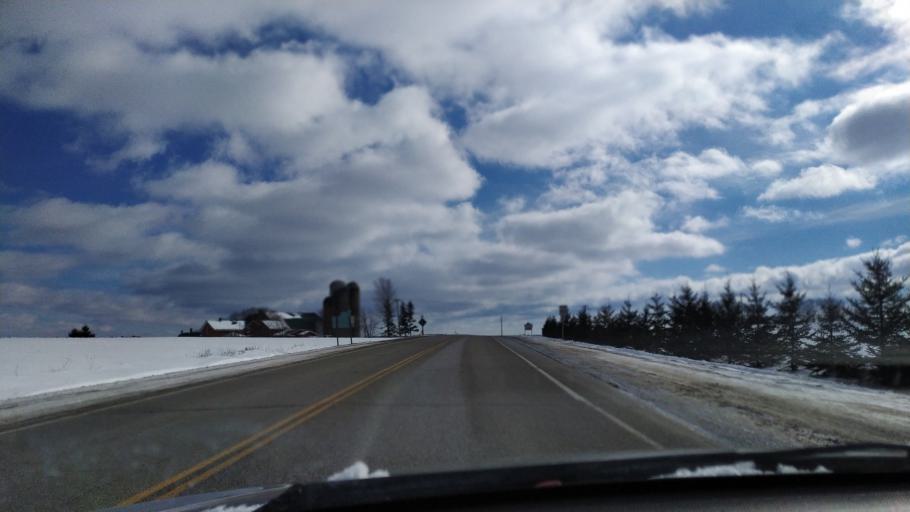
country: CA
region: Ontario
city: Waterloo
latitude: 43.5909
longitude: -80.6093
